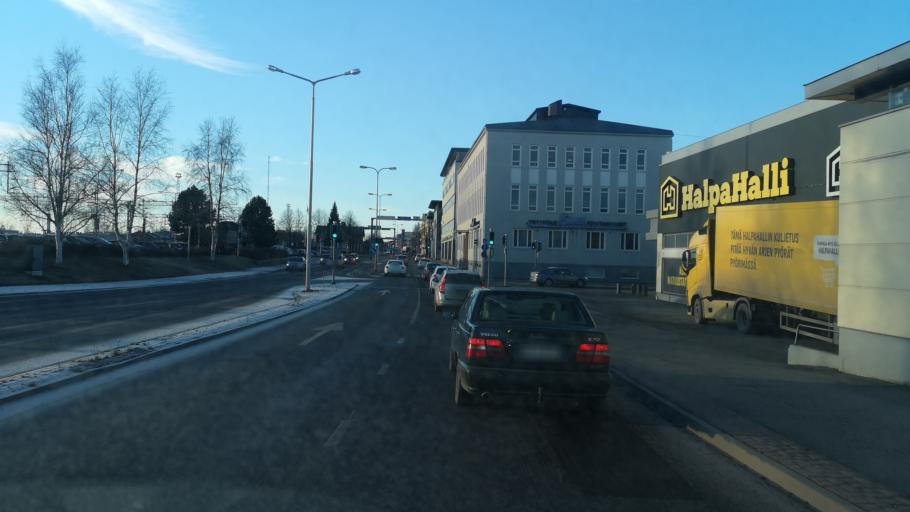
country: FI
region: Central Ostrobothnia
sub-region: Kokkola
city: Kokkola
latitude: 63.8353
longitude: 23.1363
